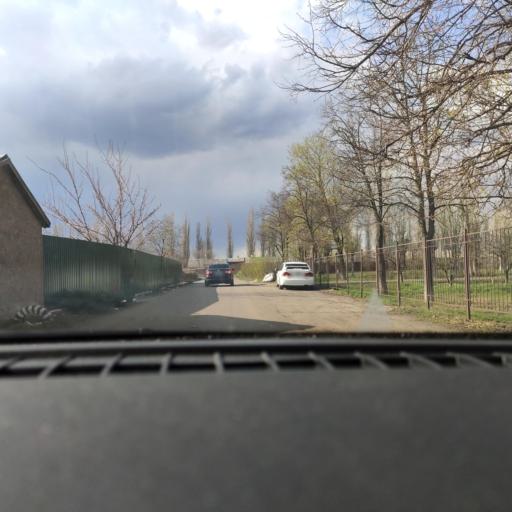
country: RU
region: Voronezj
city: Maslovka
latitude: 51.5353
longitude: 39.3325
